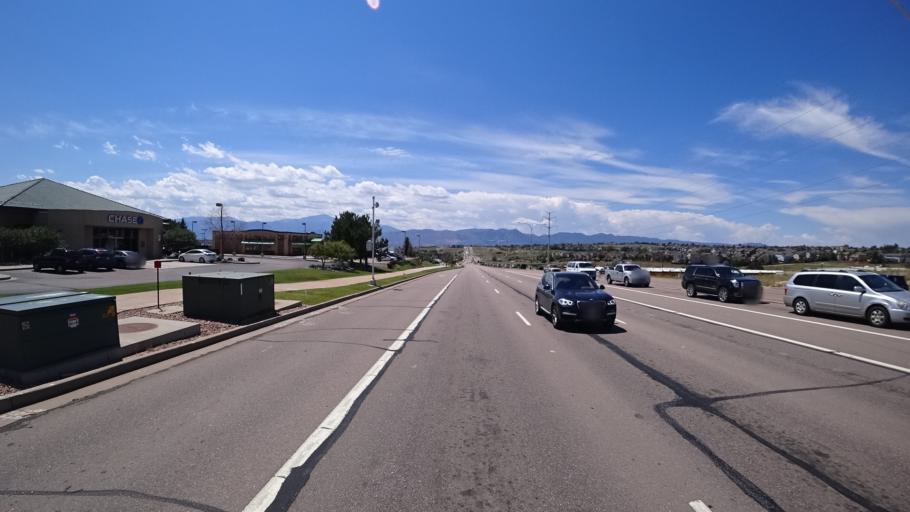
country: US
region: Colorado
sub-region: El Paso County
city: Black Forest
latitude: 38.9401
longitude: -104.7297
